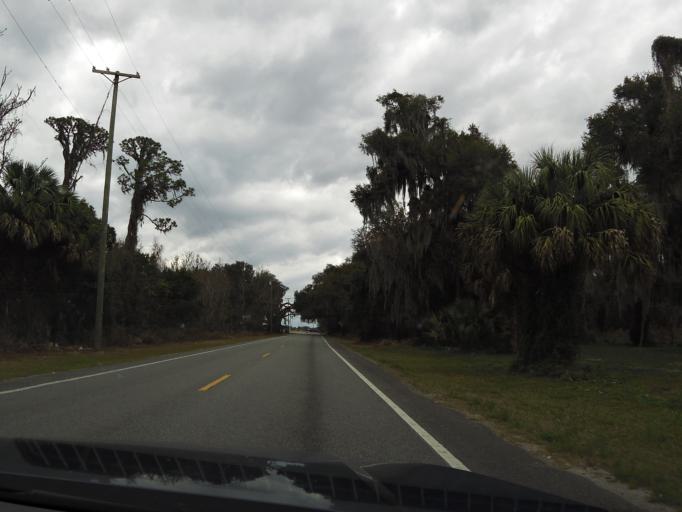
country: US
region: Florida
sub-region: Putnam County
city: Crescent City
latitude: 29.3363
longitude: -81.4979
